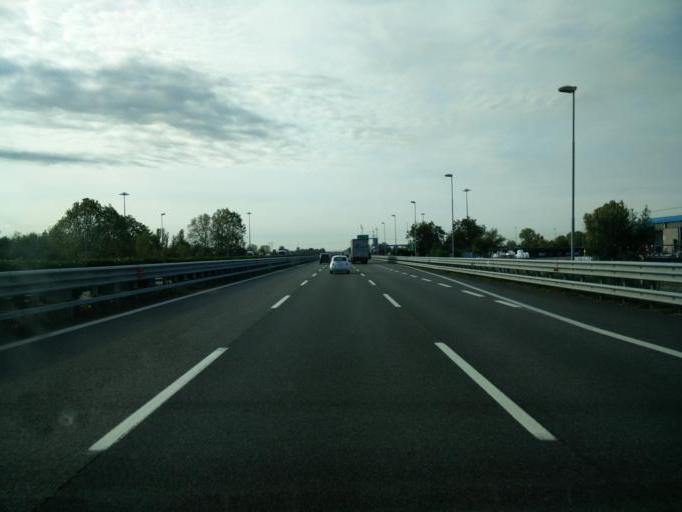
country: IT
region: Lombardy
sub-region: Provincia di Brescia
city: Montirone
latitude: 45.4492
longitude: 10.2114
